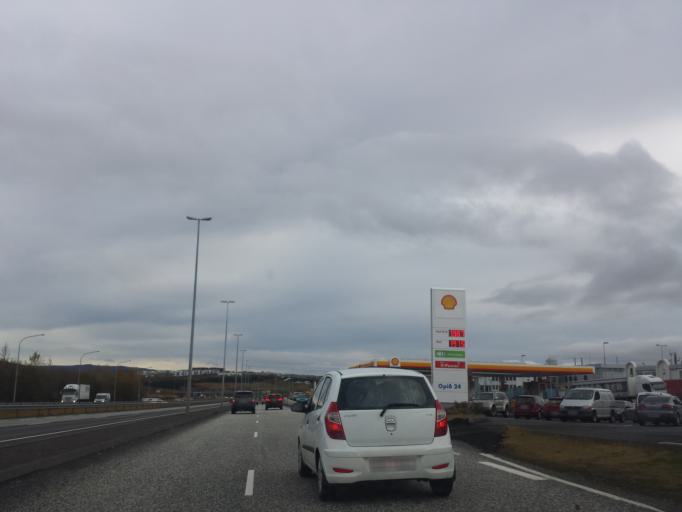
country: IS
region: Capital Region
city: Reykjavik
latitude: 64.1241
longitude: -21.8057
